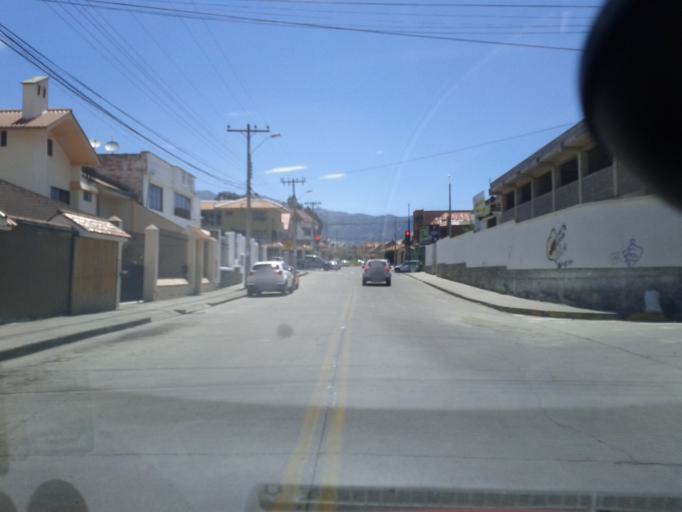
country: EC
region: Azuay
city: Cuenca
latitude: -2.9062
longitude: -79.0192
